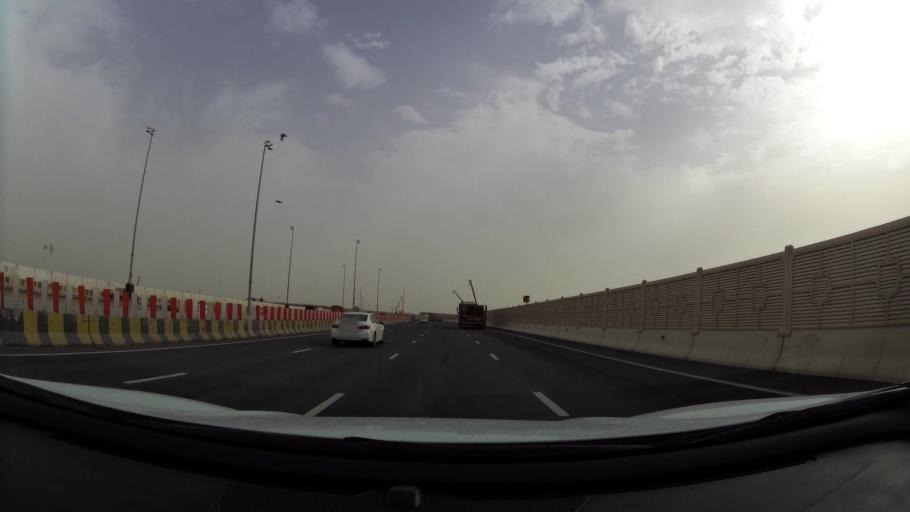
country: AE
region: Abu Dhabi
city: Abu Dhabi
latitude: 24.4515
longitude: 54.6206
